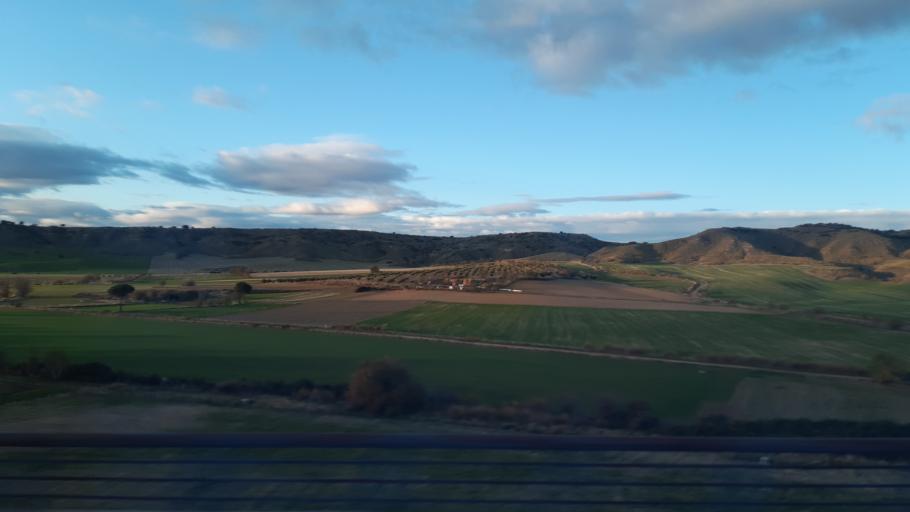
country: ES
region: Madrid
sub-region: Provincia de Madrid
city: Anchuelo
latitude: 40.4703
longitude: -3.2747
